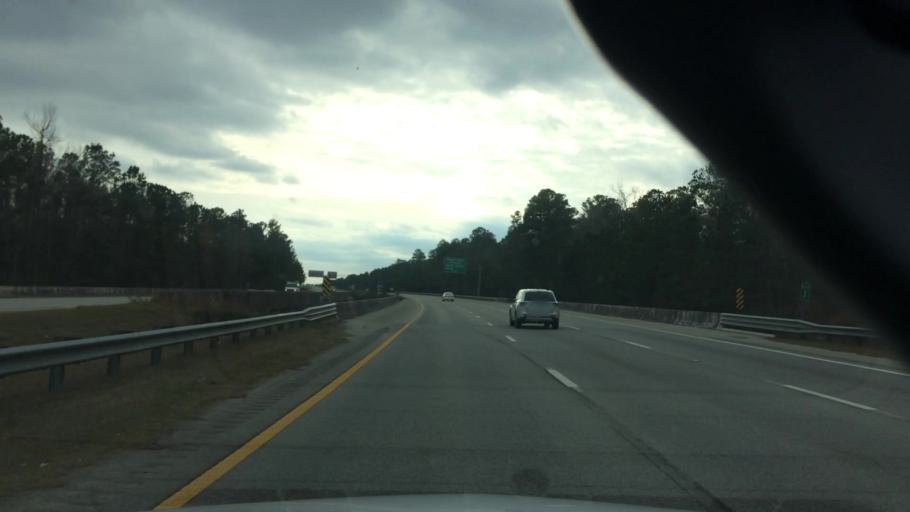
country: US
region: South Carolina
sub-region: Horry County
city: North Myrtle Beach
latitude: 33.8653
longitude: -78.6938
